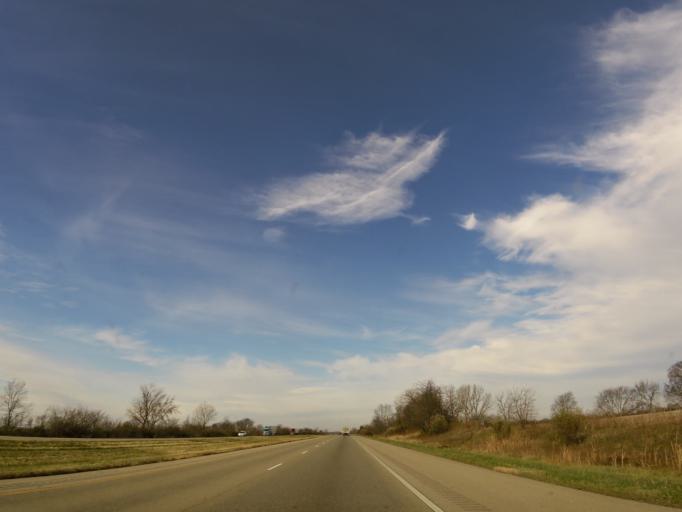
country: US
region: Illinois
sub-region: McLean County
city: Downs
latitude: 40.4019
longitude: -88.9037
